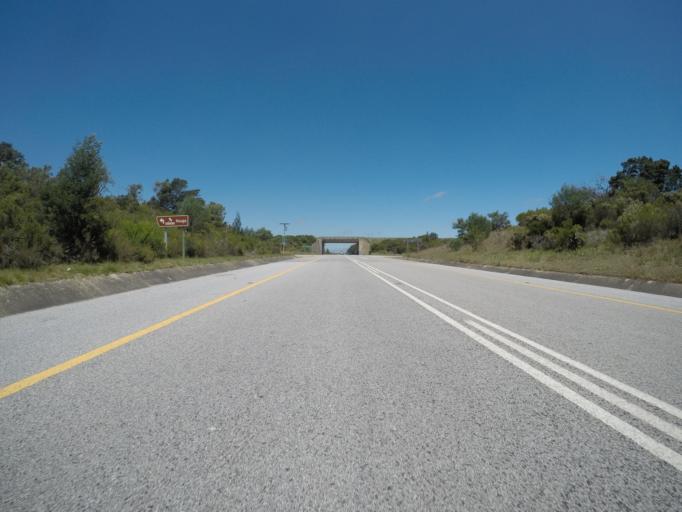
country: ZA
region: Eastern Cape
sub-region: Cacadu District Municipality
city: Kruisfontein
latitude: -34.0280
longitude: 24.5996
